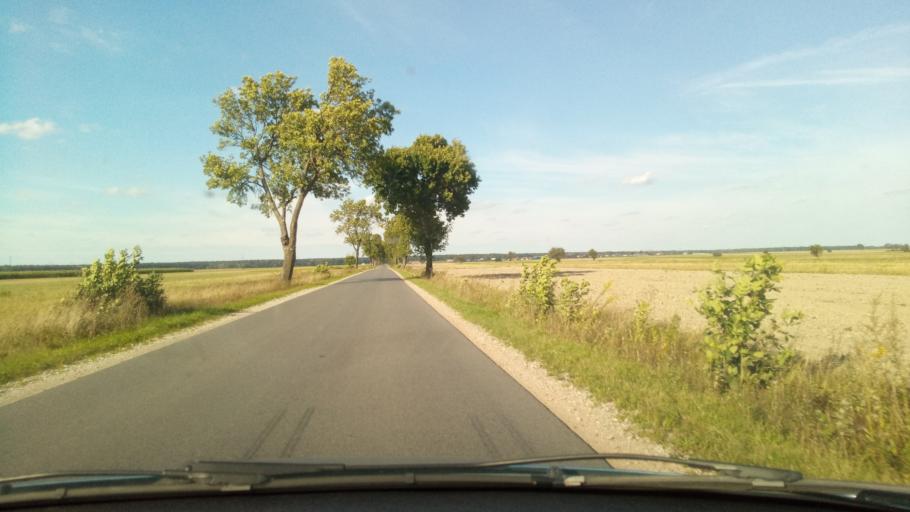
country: PL
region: Lodz Voivodeship
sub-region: Powiat piotrkowski
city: Sulejow
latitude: 51.3844
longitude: 19.8188
